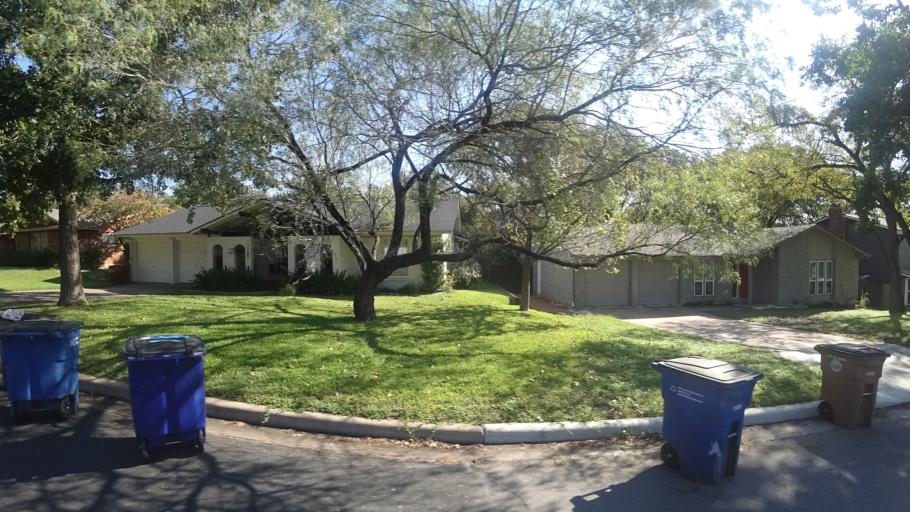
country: US
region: Texas
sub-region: Travis County
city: Austin
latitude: 30.3193
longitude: -97.6726
